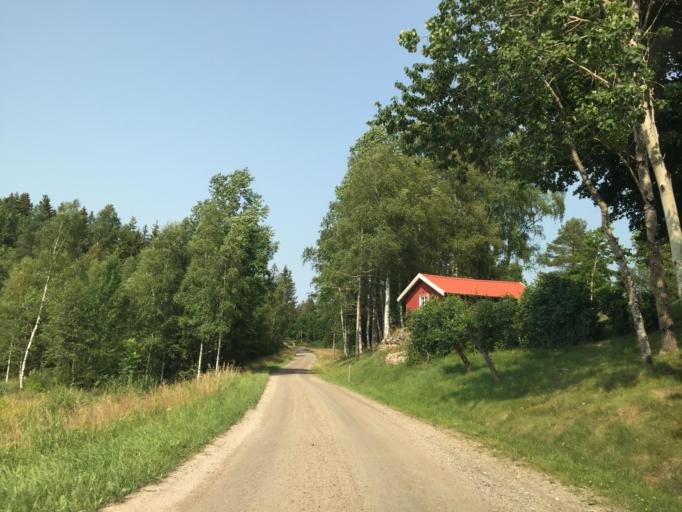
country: SE
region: Vaestra Goetaland
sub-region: Lilla Edets Kommun
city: Lilla Edet
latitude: 58.2584
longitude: 12.0967
